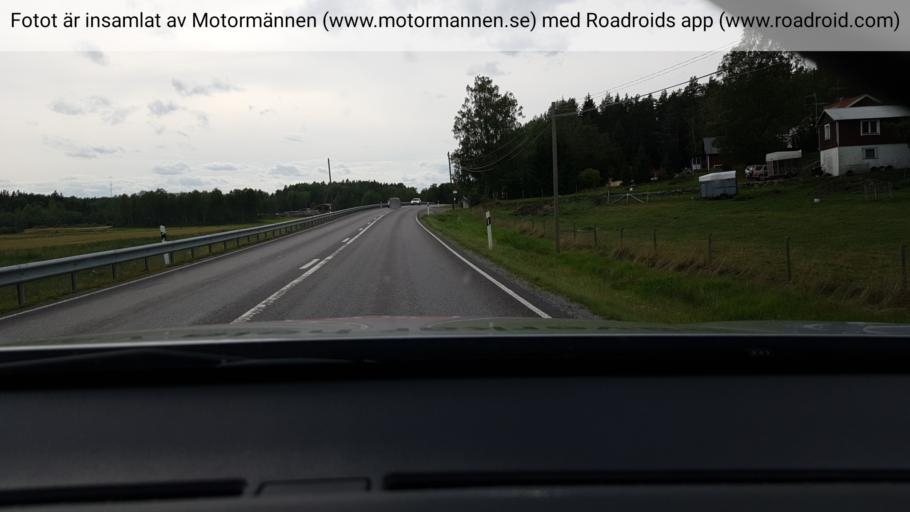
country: SE
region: Stockholm
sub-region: Sodertalje Kommun
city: Molnbo
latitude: 59.0631
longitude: 17.5119
